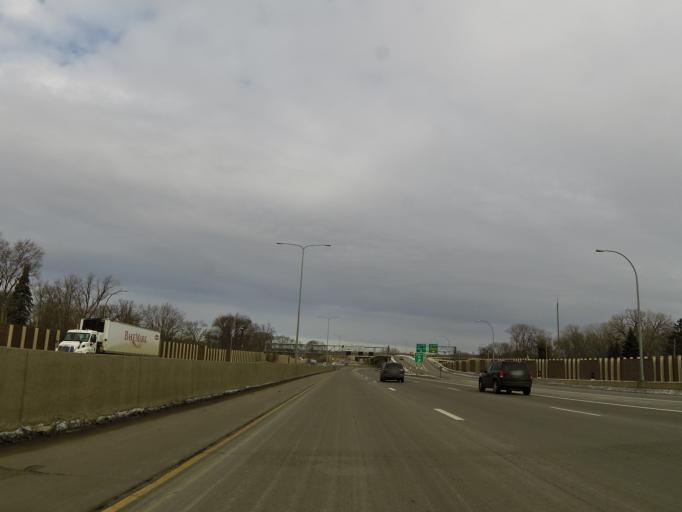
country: US
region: Minnesota
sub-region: Hennepin County
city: Richfield
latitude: 44.8845
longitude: -93.2959
